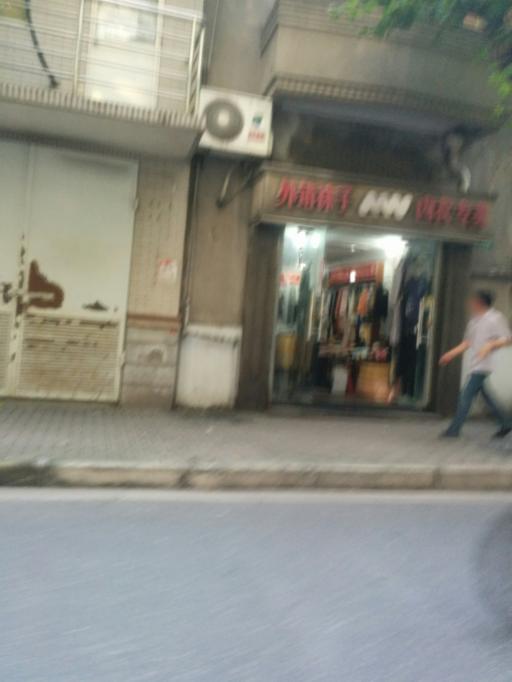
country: CN
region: Shanghai Shi
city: Shanghai
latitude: 31.2341
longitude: 121.4581
